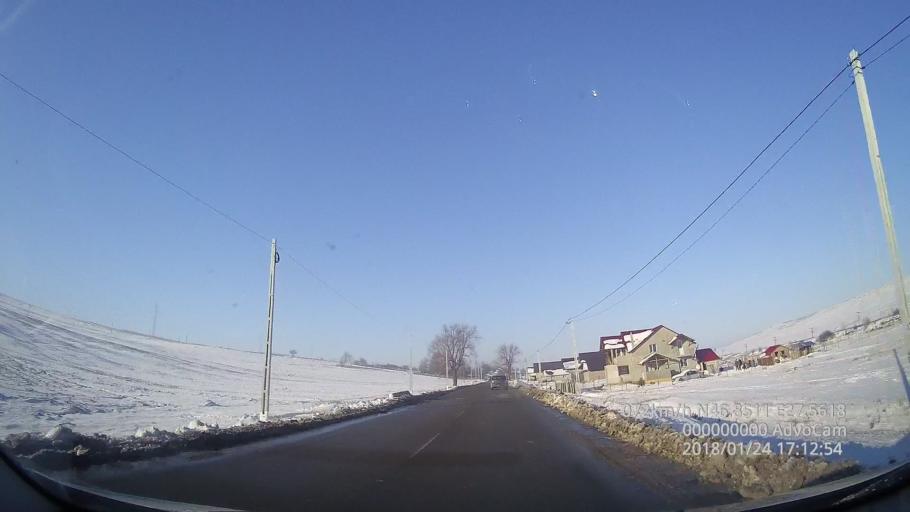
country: RO
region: Vaslui
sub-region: Comuna Rebricea
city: Rebricea
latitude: 46.8517
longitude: 27.5617
